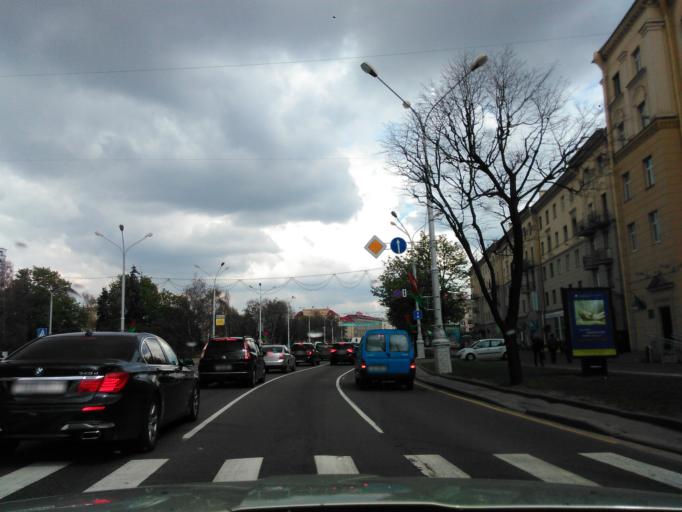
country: BY
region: Minsk
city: Minsk
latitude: 53.9138
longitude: 27.5812
